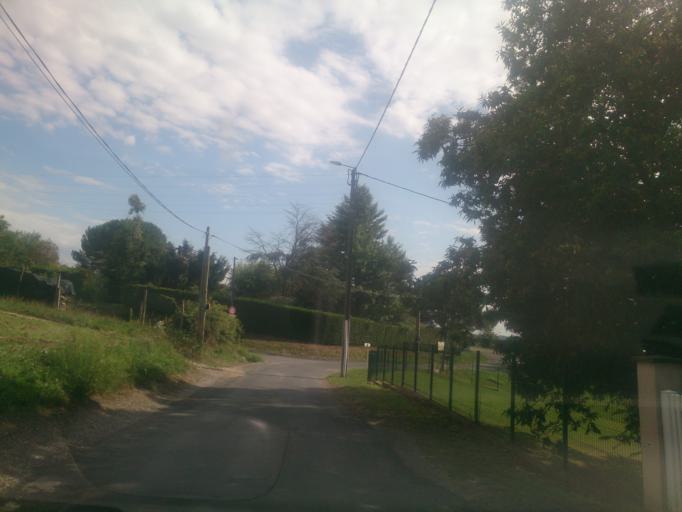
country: FR
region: Limousin
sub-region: Departement de la Correze
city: Malemort-sur-Correze
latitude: 45.1796
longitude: 1.5437
